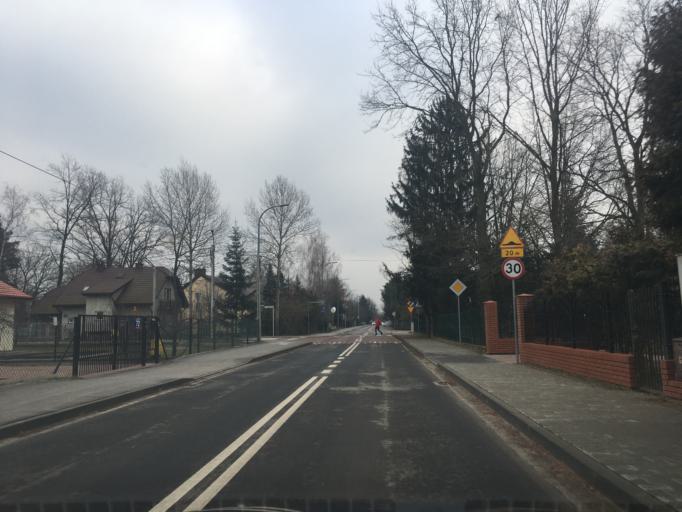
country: PL
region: Masovian Voivodeship
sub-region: Powiat piaseczynski
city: Piaseczno
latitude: 52.0608
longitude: 20.9790
